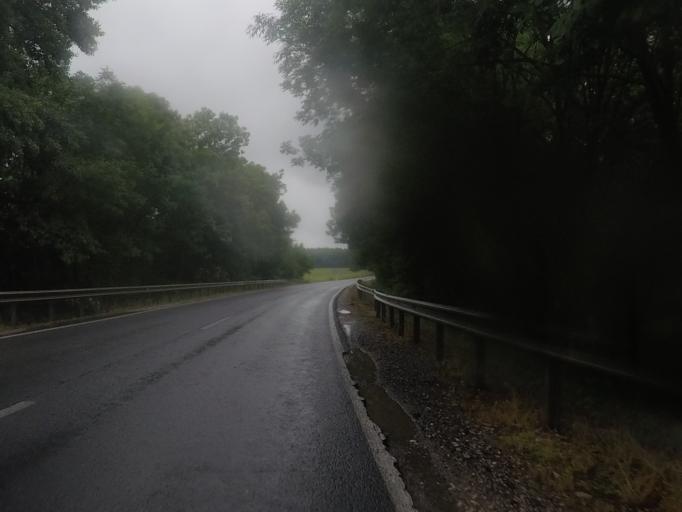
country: HU
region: Veszprem
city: Zirc
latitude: 47.2293
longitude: 17.9020
